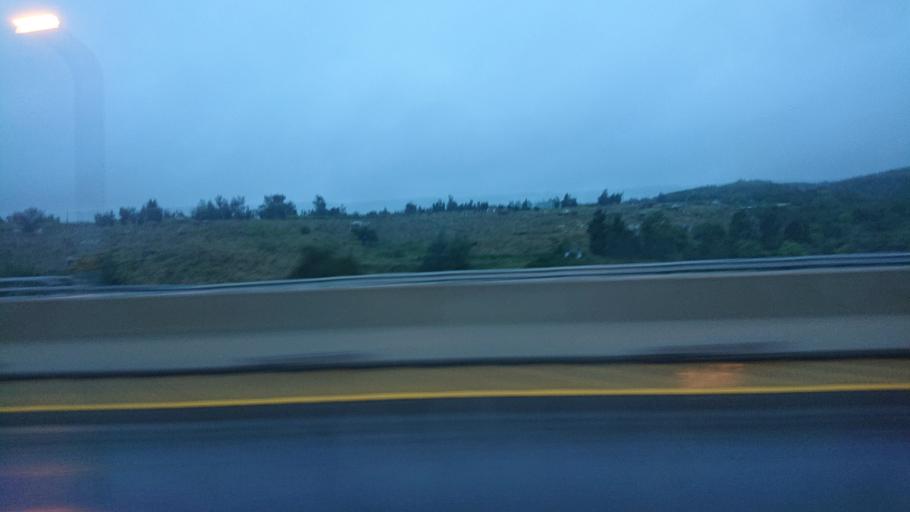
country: TW
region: Taiwan
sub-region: Miaoli
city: Miaoli
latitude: 24.5650
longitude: 120.7142
